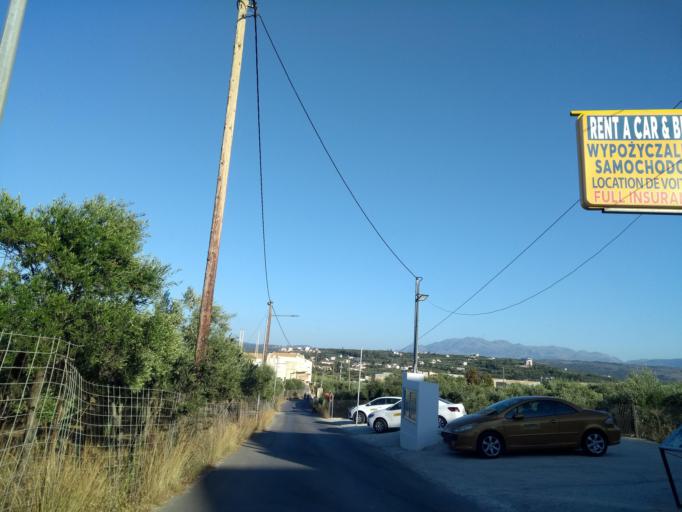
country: GR
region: Crete
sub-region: Nomos Chanias
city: Kalivai
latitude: 35.4672
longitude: 24.1537
